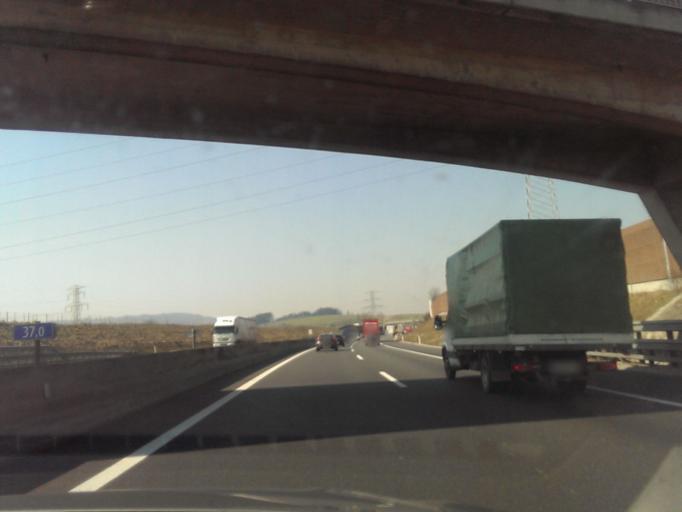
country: AT
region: Upper Austria
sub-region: Politischer Bezirk Vocklabruck
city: Wolfsegg am Hausruck
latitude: 48.1760
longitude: 13.7042
